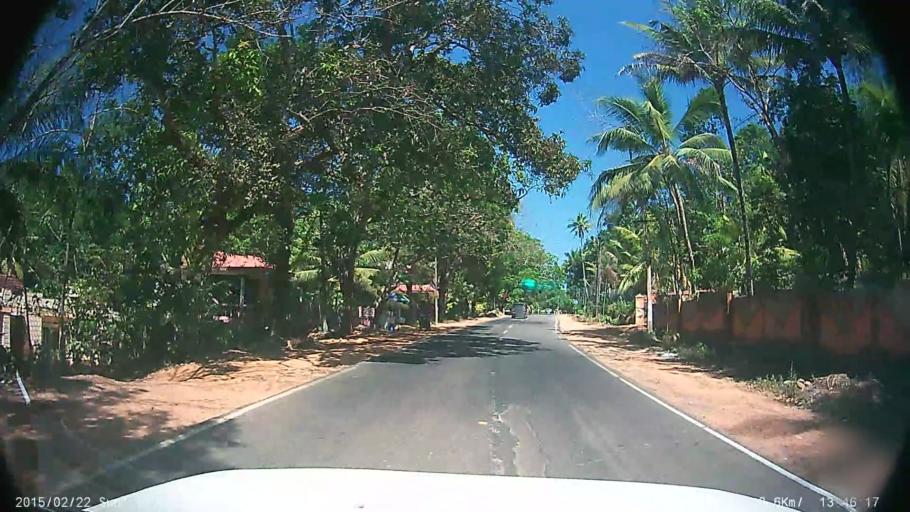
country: IN
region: Kerala
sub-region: Kottayam
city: Changanacheri
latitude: 9.4852
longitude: 76.6122
